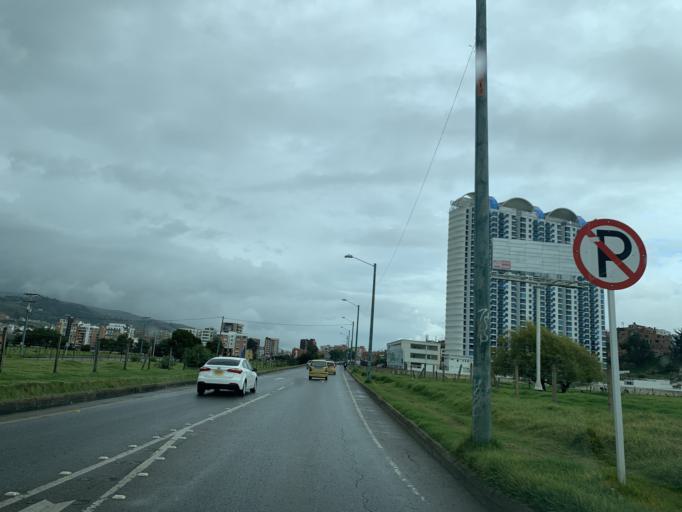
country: CO
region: Boyaca
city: Tunja
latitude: 5.5375
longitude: -73.3522
